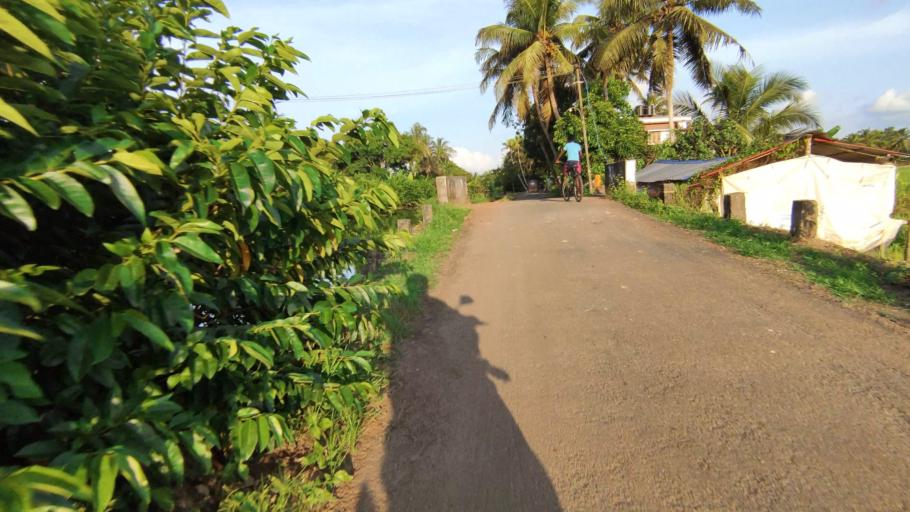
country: IN
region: Kerala
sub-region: Kottayam
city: Kottayam
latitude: 9.5886
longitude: 76.4499
